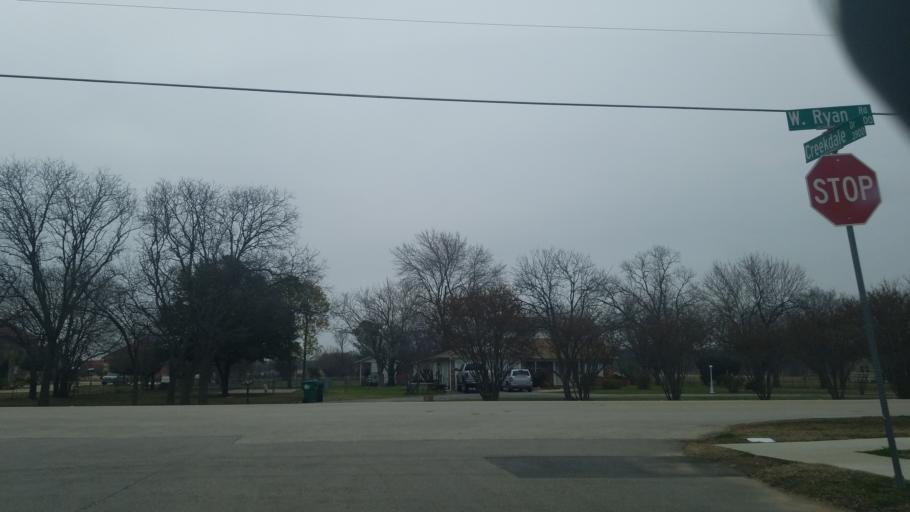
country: US
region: Texas
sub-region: Denton County
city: Denton
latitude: 33.1613
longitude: -97.1366
